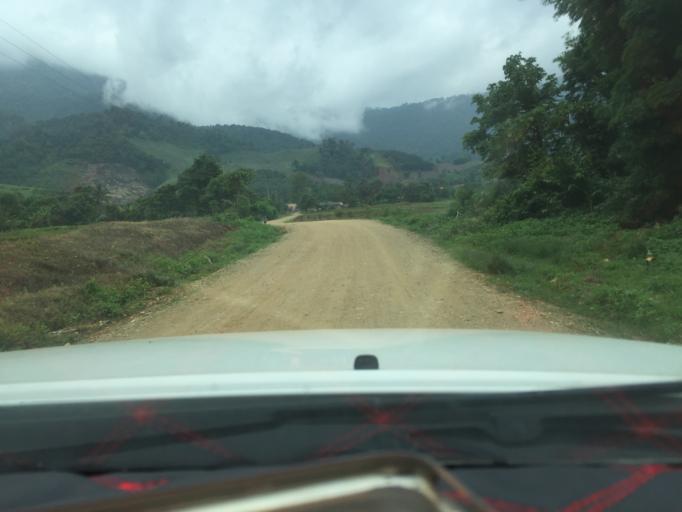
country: TH
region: Phayao
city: Phu Sang
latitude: 19.7431
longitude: 100.4352
